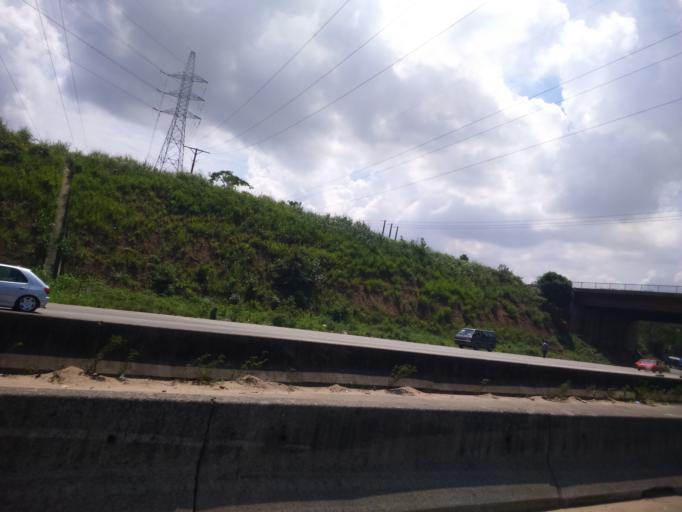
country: CI
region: Lagunes
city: Abobo
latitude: 5.3639
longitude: -4.0315
